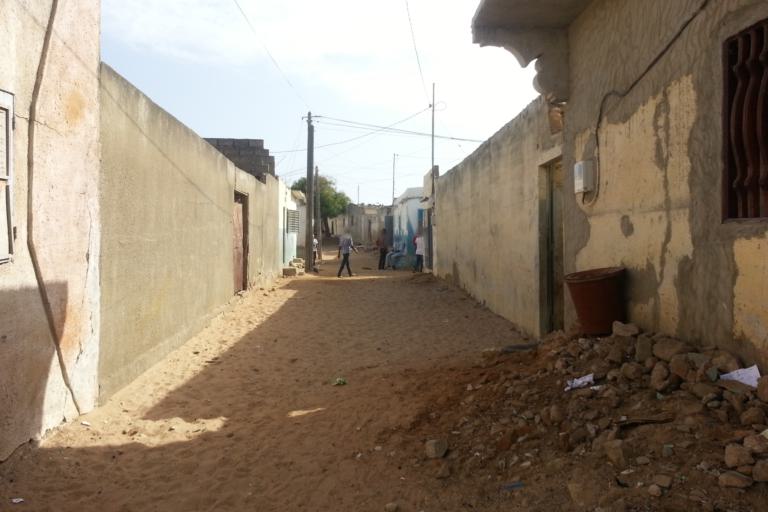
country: SN
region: Dakar
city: Pikine
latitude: 14.7726
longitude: -17.3812
